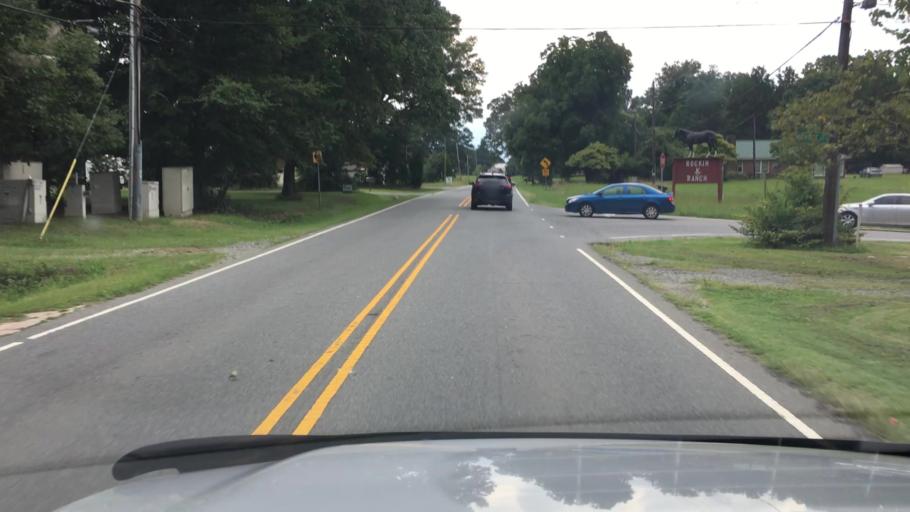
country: US
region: North Carolina
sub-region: Mecklenburg County
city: Huntersville
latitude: 35.3336
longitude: -80.8743
